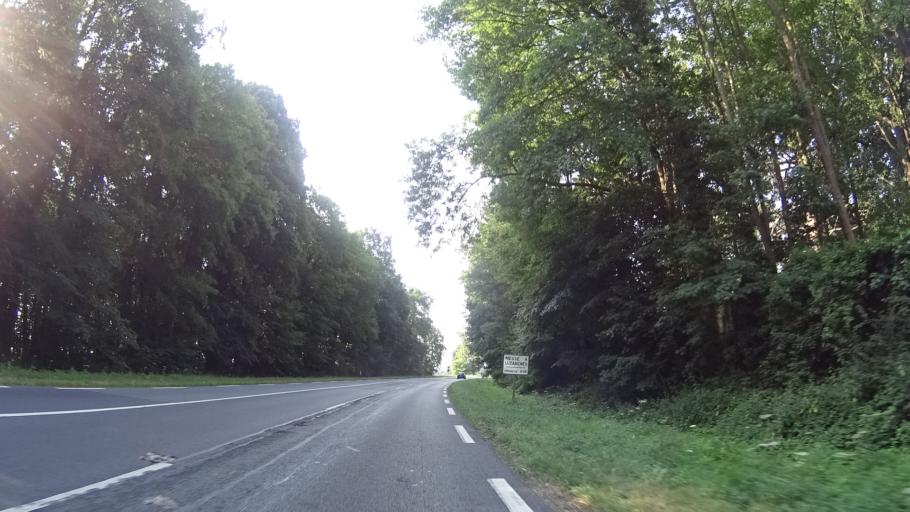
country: FR
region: Ile-de-France
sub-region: Departement du Val-d'Oise
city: Luzarches
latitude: 49.1163
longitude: 2.4294
